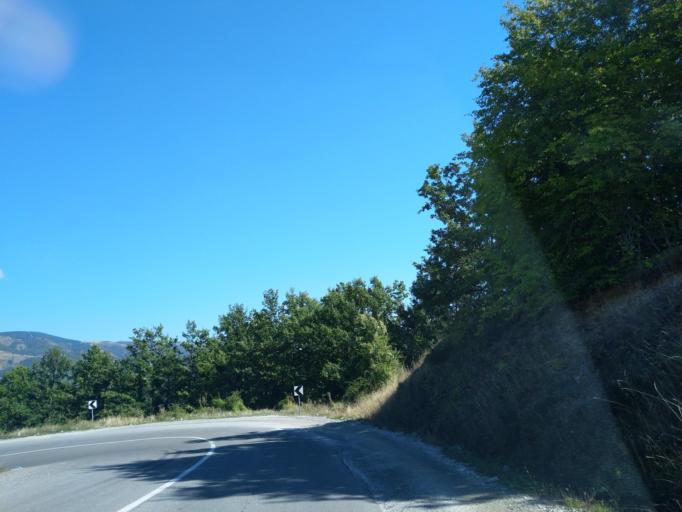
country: RS
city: Sokolovica
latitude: 43.2524
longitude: 20.2469
